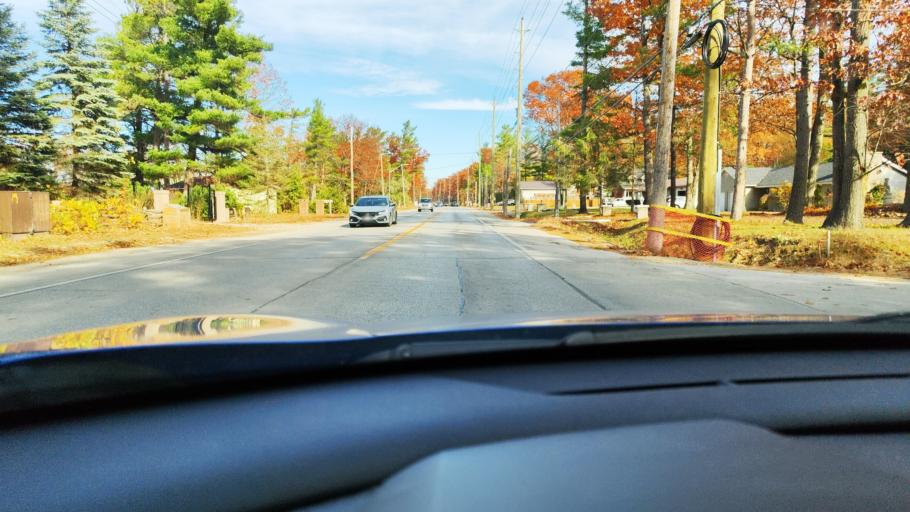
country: CA
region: Ontario
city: Wasaga Beach
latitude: 44.5015
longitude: -80.0361
